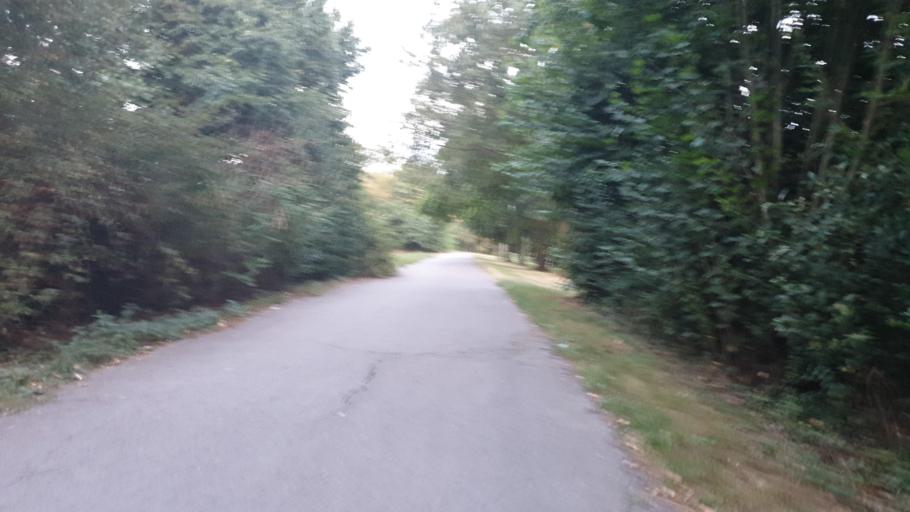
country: DE
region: North Rhine-Westphalia
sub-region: Regierungsbezirk Koln
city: Bergheim
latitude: 50.9474
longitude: 6.6339
